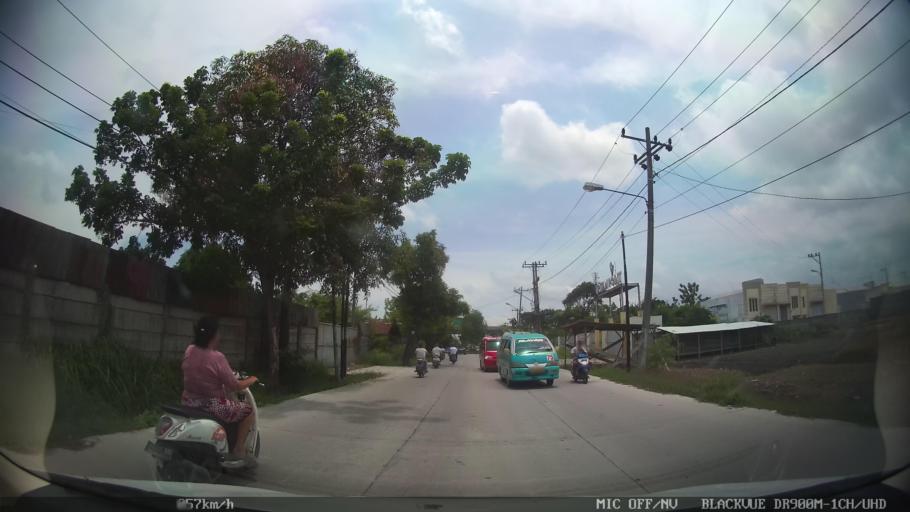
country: ID
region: North Sumatra
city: Labuhan Deli
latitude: 3.6922
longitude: 98.6805
